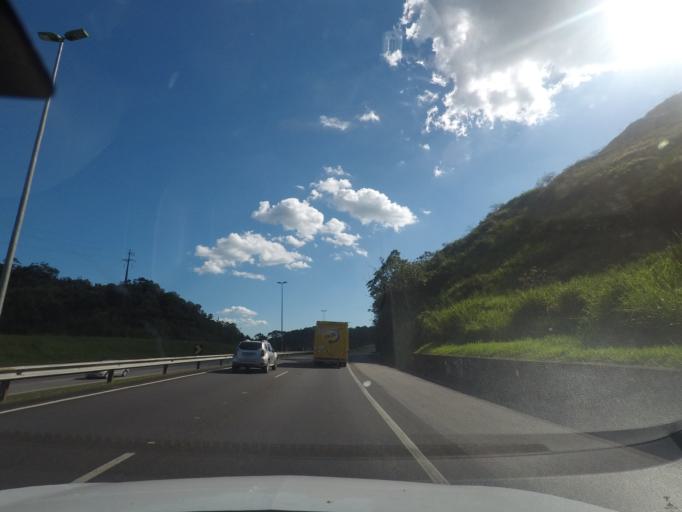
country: BR
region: Rio de Janeiro
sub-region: Guapimirim
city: Guapimirim
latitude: -22.5780
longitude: -43.0104
